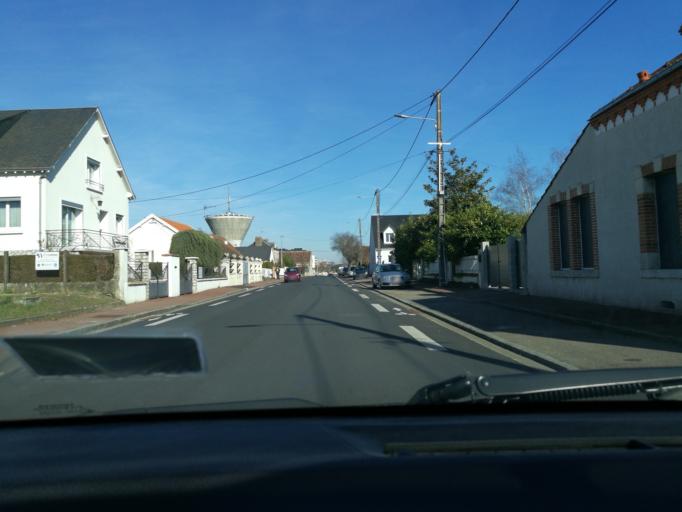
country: FR
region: Centre
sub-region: Departement du Loiret
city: Saint-Jean-de-la-Ruelle
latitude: 47.9187
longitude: 1.8756
